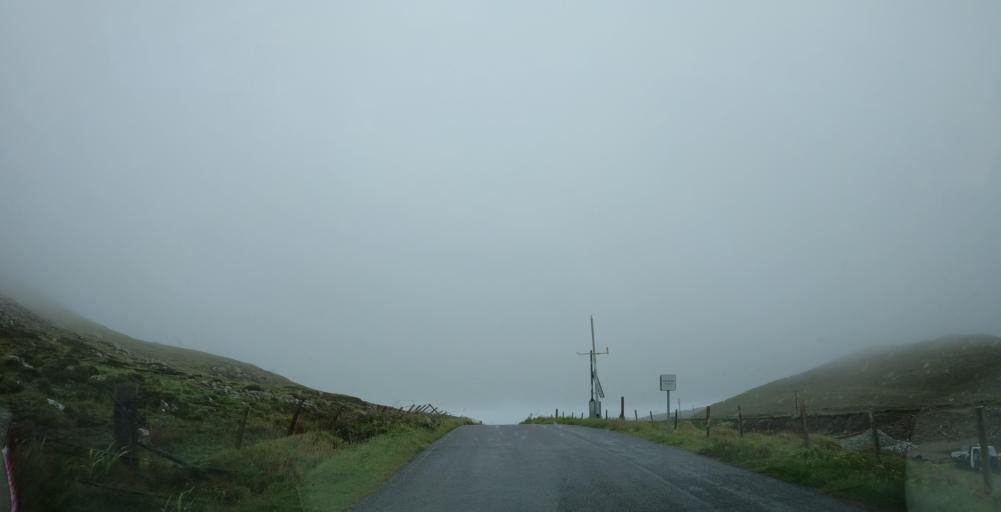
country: GB
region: Scotland
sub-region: Eilean Siar
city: Barra
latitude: 56.9601
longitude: -7.4655
